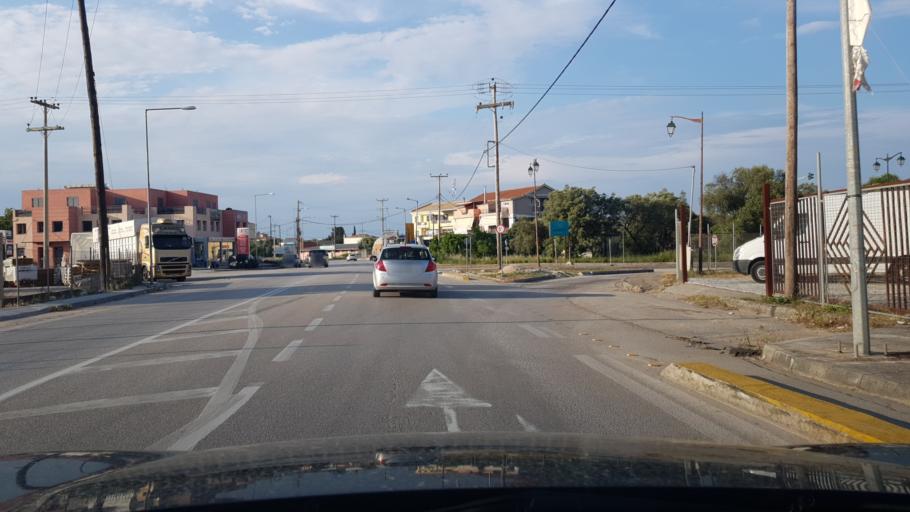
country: GR
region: Ionian Islands
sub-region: Lefkada
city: Lefkada
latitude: 38.8239
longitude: 20.7025
